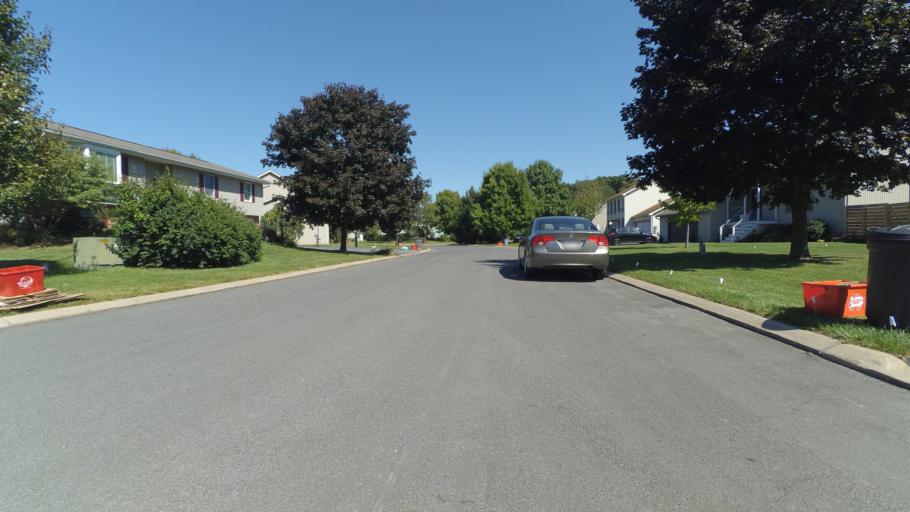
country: US
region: Pennsylvania
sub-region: Centre County
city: Pine Grove Mills
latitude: 40.7609
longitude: -77.8900
